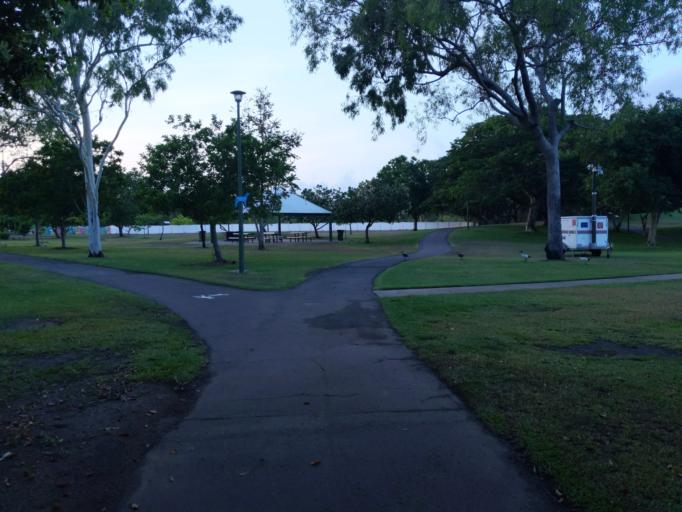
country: AU
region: Northern Territory
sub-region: Darwin
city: Nightcliff
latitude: -12.3871
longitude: 130.8680
